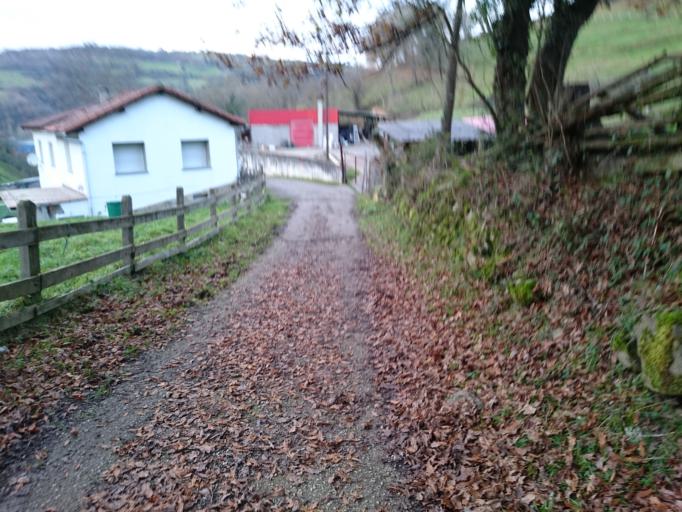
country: ES
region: Asturias
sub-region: Province of Asturias
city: Oviedo
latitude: 43.3174
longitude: -5.7982
